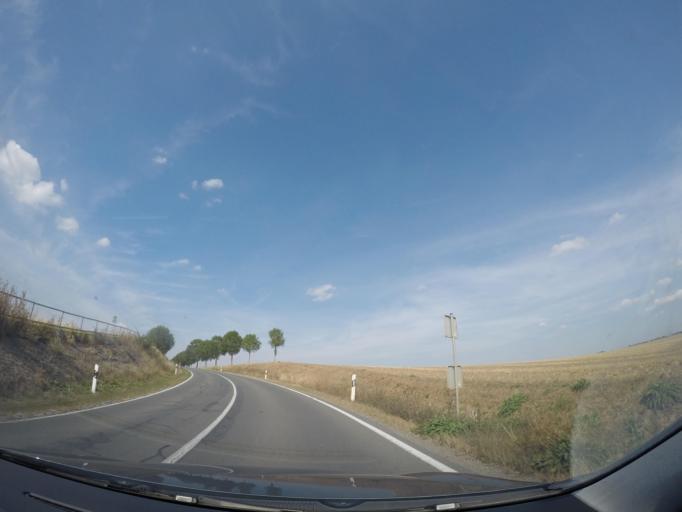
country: DE
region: Saxony-Anhalt
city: Heudeber
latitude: 51.9608
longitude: 10.8331
